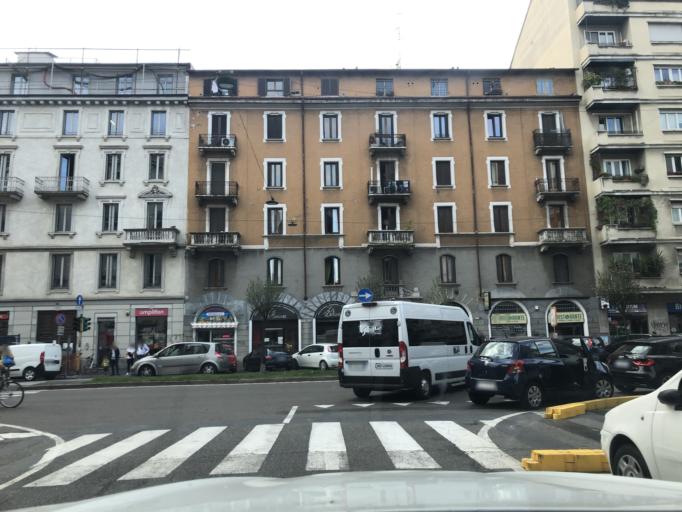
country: IT
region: Lombardy
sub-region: Citta metropolitana di Milano
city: Sesto San Giovanni
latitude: 45.4948
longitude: 9.2200
